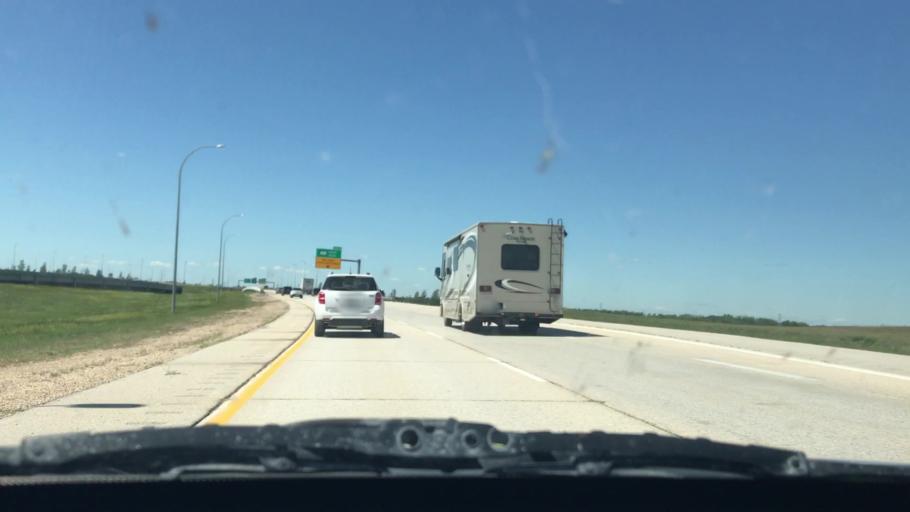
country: CA
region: Manitoba
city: Winnipeg
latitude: 49.8297
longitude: -96.9507
